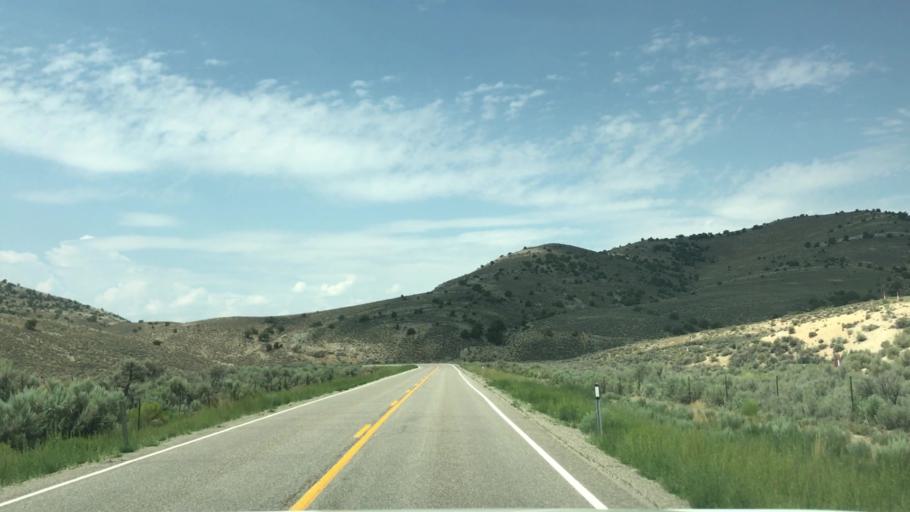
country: US
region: Nevada
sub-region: White Pine County
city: Ely
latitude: 39.3516
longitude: -115.3743
